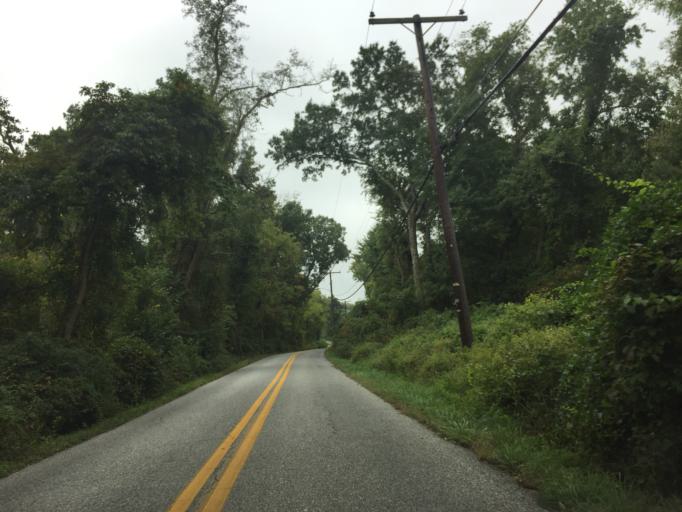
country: US
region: Maryland
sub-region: Baltimore County
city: Bowleys Quarters
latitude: 39.3711
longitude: -76.3896
